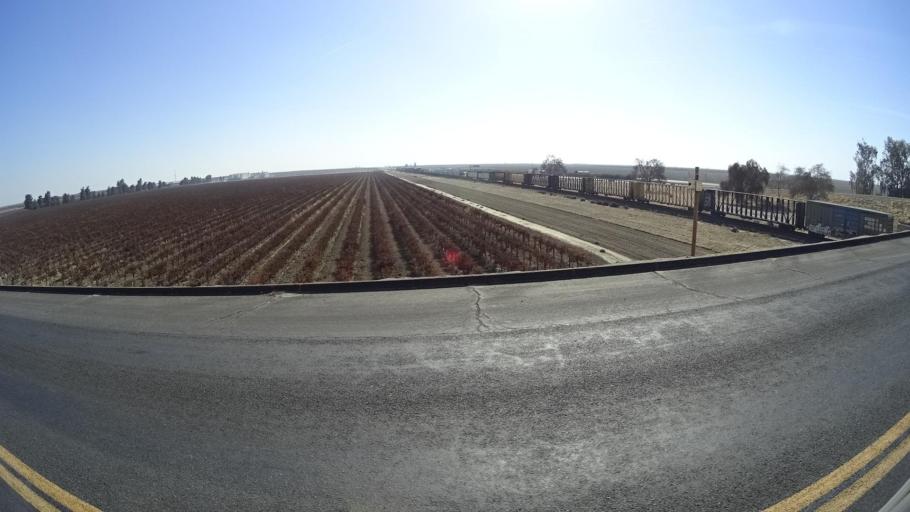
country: US
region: California
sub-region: Kern County
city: McFarland
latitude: 35.6456
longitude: -119.2184
